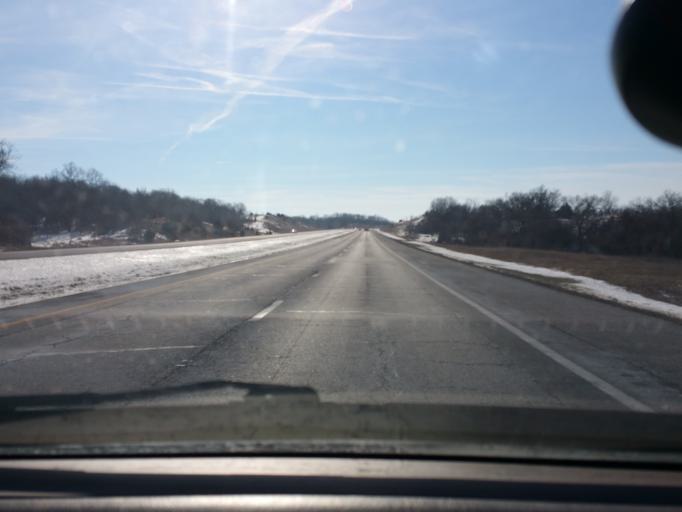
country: US
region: Missouri
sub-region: Harrison County
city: Bethany
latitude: 40.1898
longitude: -94.0147
